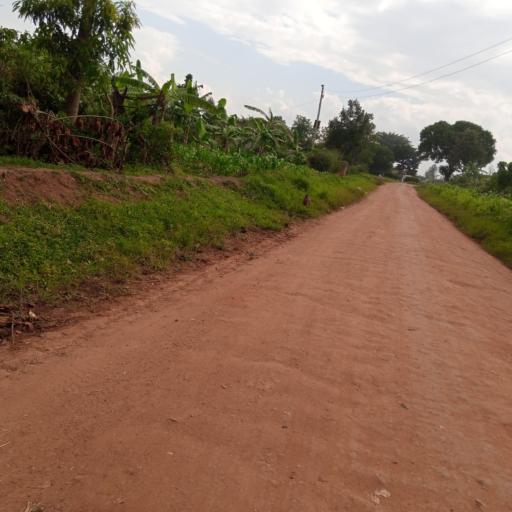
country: UG
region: Eastern Region
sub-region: Mbale District
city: Mbale
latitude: 1.0848
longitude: 34.1824
